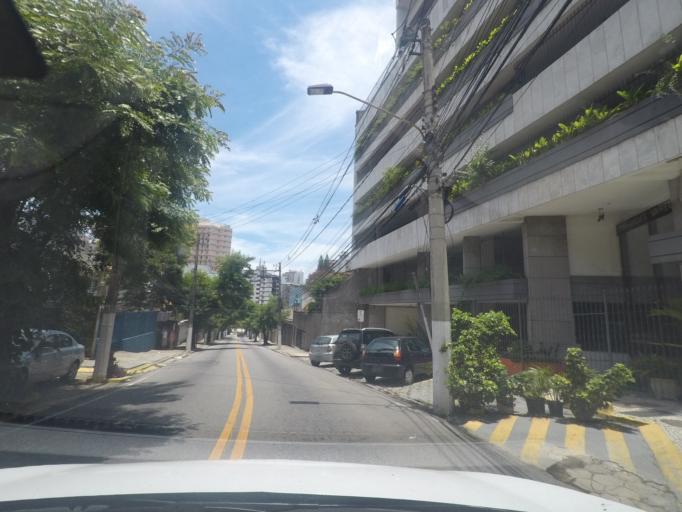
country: BR
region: Rio de Janeiro
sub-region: Niteroi
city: Niteroi
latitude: -22.9006
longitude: -43.1202
